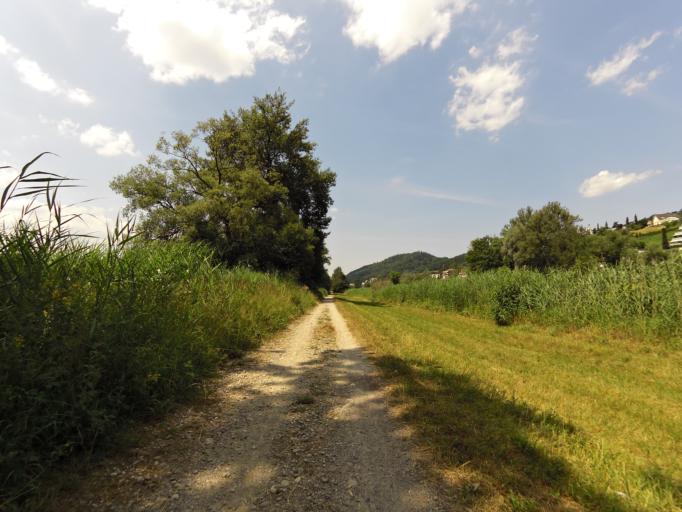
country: CH
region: Zurich
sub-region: Bezirk Dietikon
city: Geroldswil
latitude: 47.4235
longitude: 8.3993
